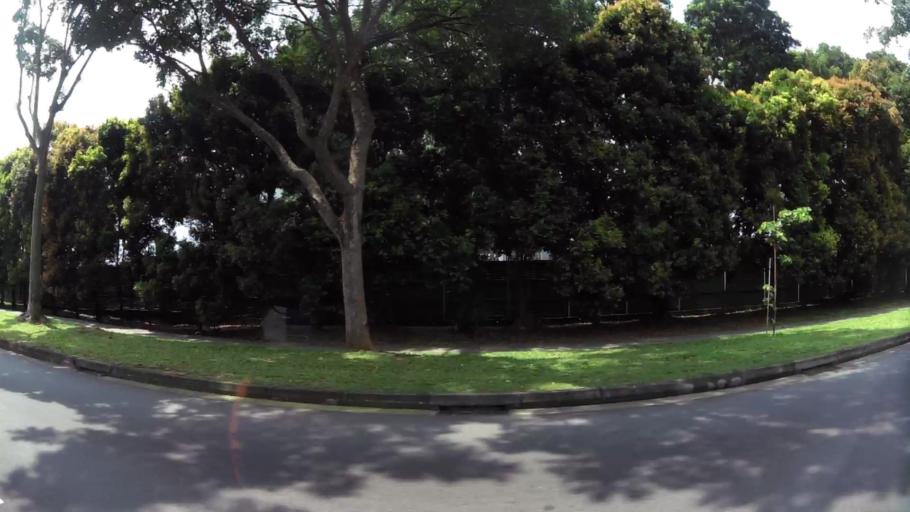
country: MY
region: Johor
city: Kampung Pasir Gudang Baru
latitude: 1.3813
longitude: 103.9784
